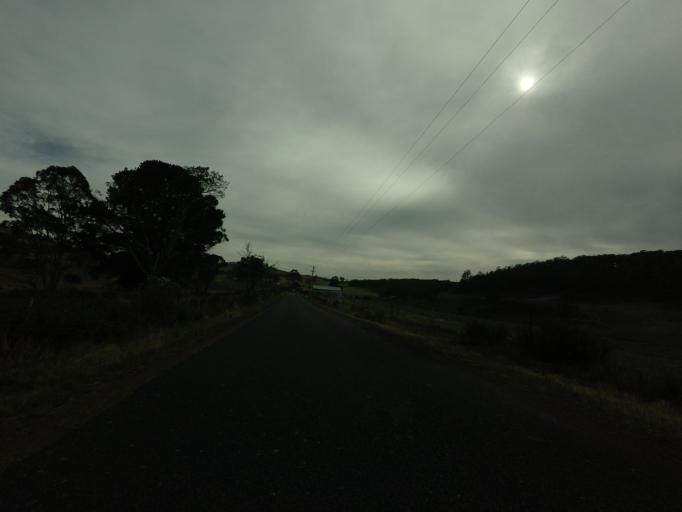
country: AU
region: Tasmania
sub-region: Sorell
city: Sorell
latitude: -42.4637
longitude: 147.5712
